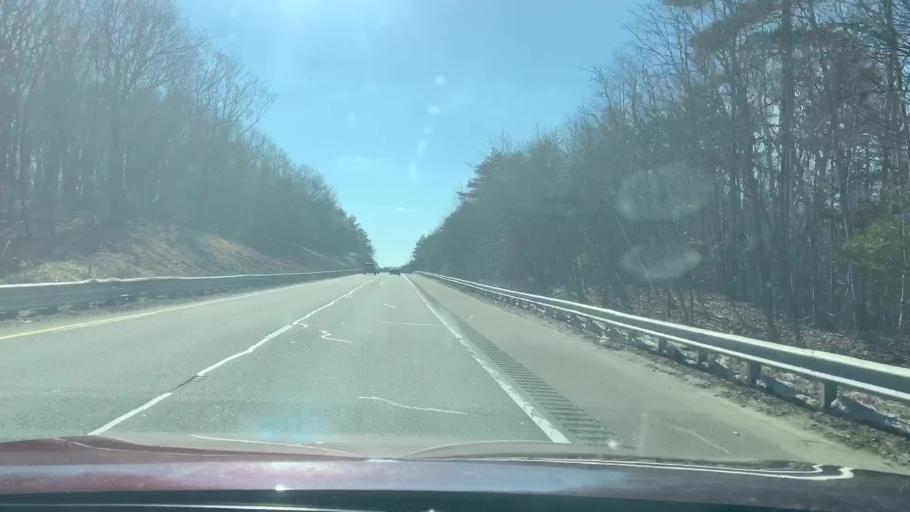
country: US
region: Massachusetts
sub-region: Essex County
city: Essex
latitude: 42.6074
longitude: -70.7386
